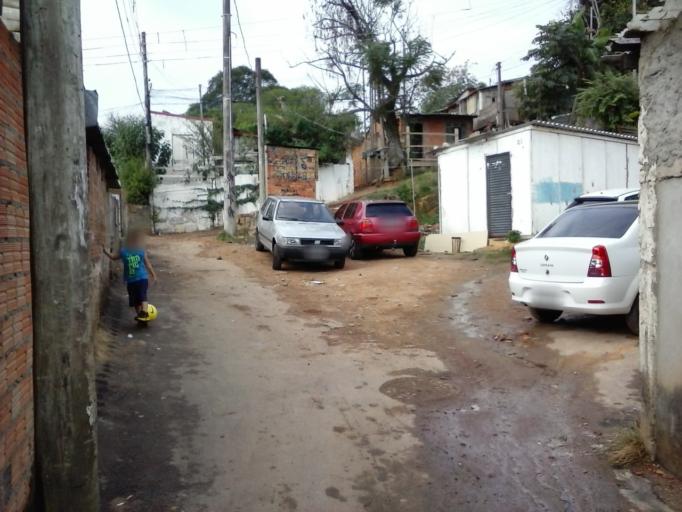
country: BR
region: Rio Grande do Sul
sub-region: Porto Alegre
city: Porto Alegre
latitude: -30.0590
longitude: -51.1432
